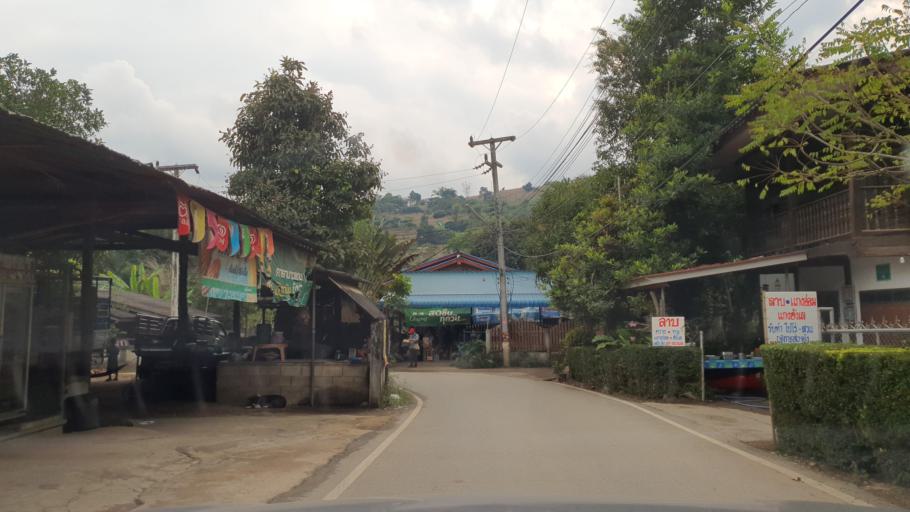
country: TH
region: Chiang Mai
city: Mae Wang
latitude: 18.6597
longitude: 98.6614
